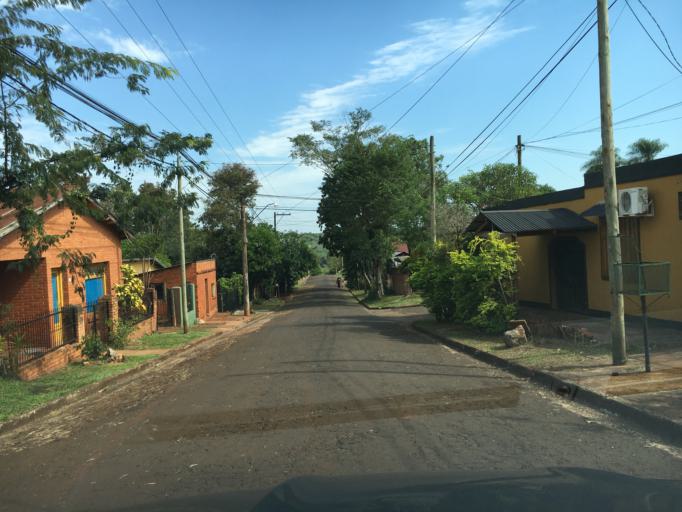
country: AR
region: Misiones
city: Puerto Rico
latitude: -26.8092
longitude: -55.0283
